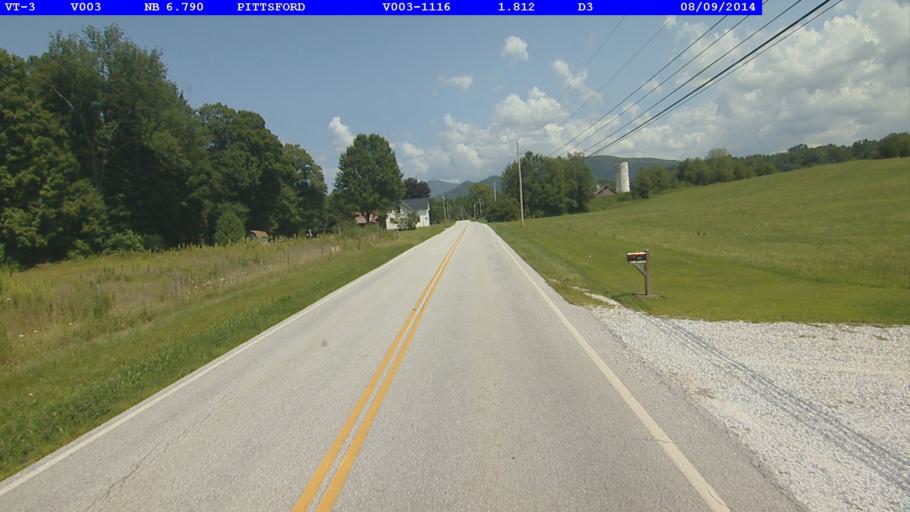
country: US
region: Vermont
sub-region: Rutland County
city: Rutland
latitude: 43.6889
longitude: -73.0201
